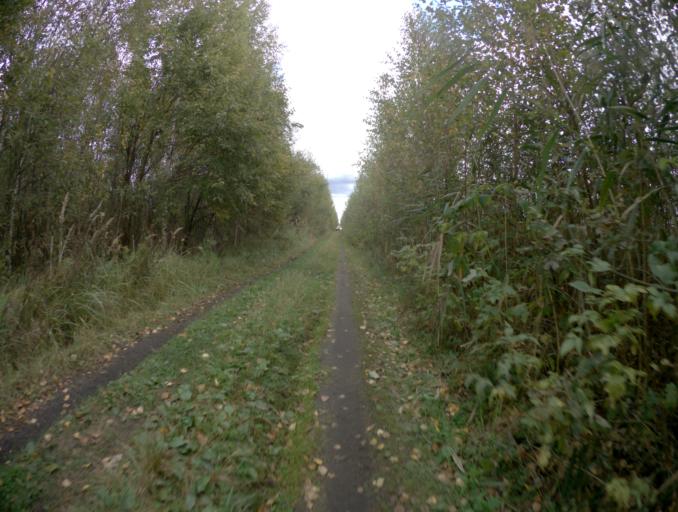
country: RU
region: Vladimir
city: Urshel'skiy
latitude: 55.7486
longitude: 40.0942
